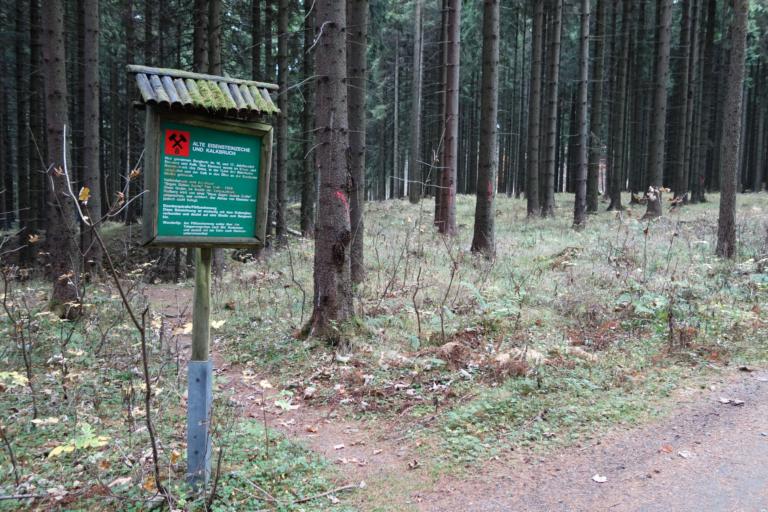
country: DE
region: Saxony
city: Kurort Oberwiesenthal
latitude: 50.4570
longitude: 12.9847
